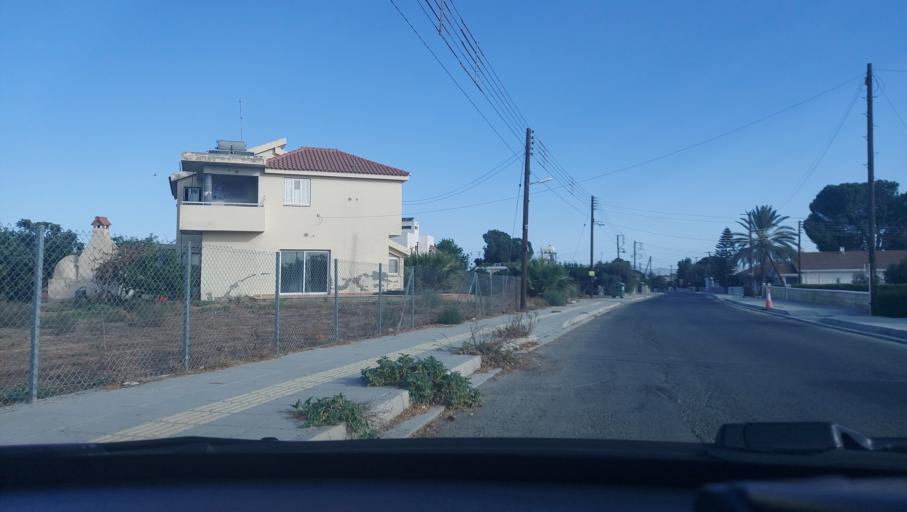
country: CY
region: Lefkosia
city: Pano Deftera
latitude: 35.0726
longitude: 33.2618
